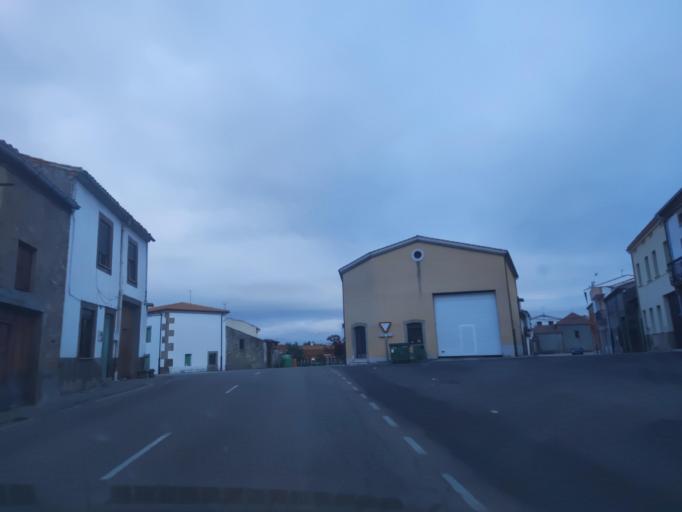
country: ES
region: Castille and Leon
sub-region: Provincia de Salamanca
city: Lumbrales
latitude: 40.9345
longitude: -6.7165
